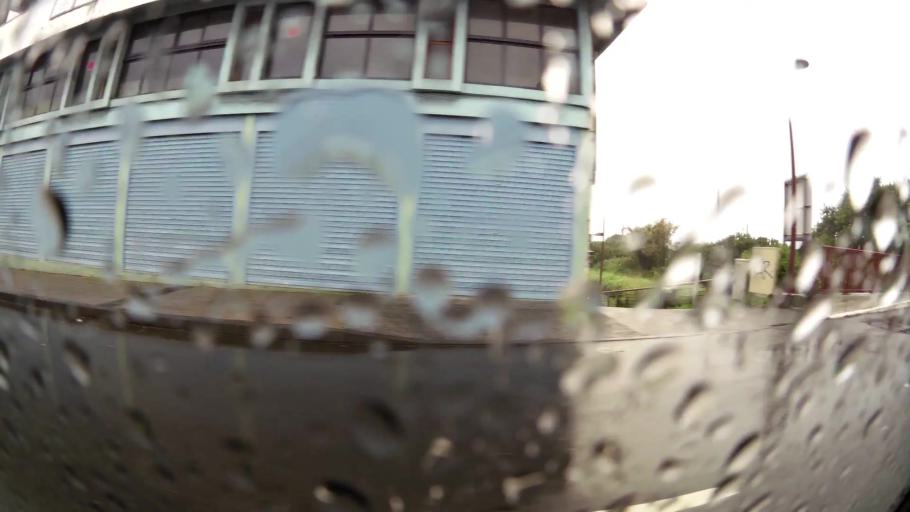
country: RE
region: Reunion
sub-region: Reunion
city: Saint-Benoit
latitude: -21.0348
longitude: 55.7143
